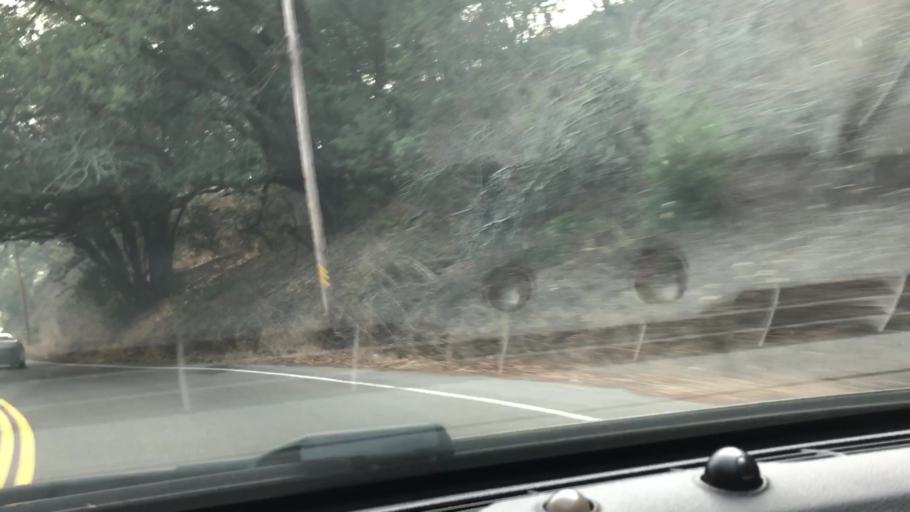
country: US
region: California
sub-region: Contra Costa County
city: Orinda
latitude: 37.8784
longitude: -122.2213
